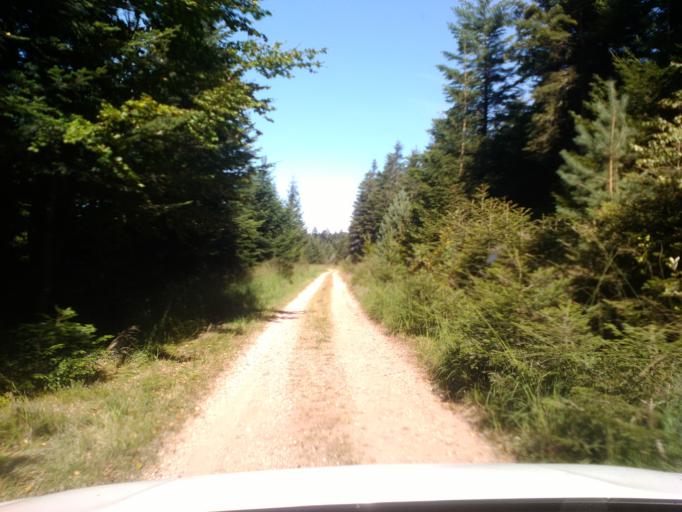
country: FR
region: Lorraine
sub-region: Departement des Vosges
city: Senones
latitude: 48.4270
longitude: 6.9896
